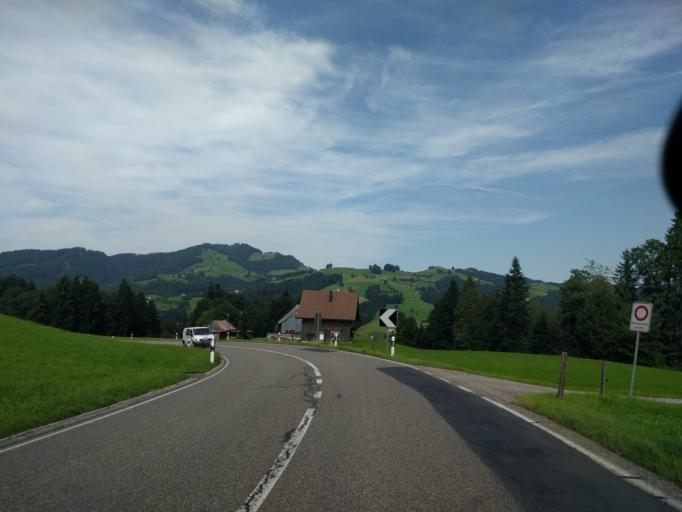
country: CH
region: Saint Gallen
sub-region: Wahlkreis Toggenburg
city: Wattwil
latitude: 47.2854
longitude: 9.0829
